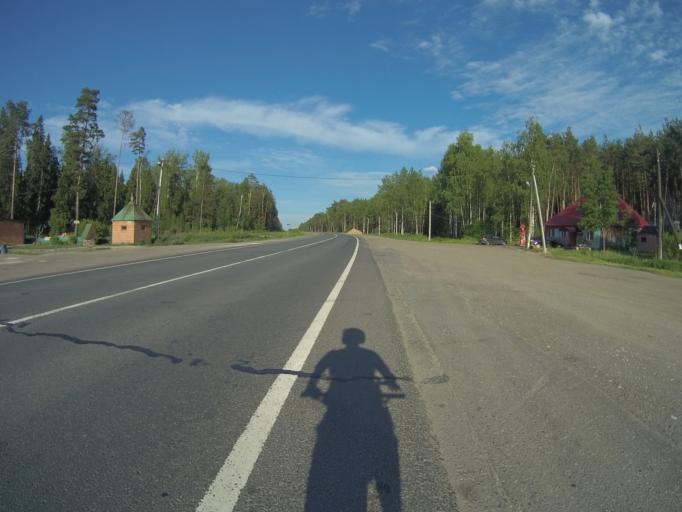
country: RU
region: Vladimir
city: Kameshkovo
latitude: 56.1933
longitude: 40.9284
